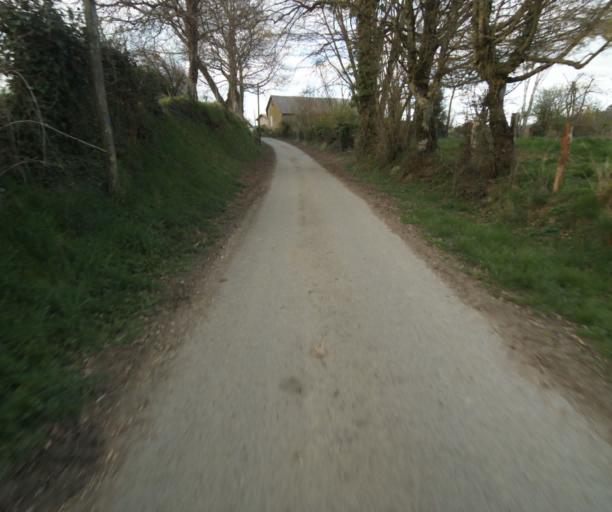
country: FR
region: Limousin
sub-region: Departement de la Correze
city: Saint-Clement
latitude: 45.3582
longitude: 1.6209
